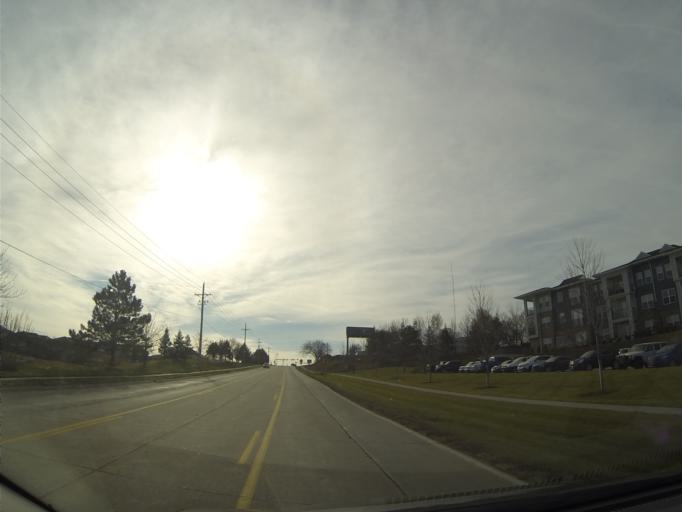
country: US
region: Nebraska
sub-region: Douglas County
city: Elkhorn
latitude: 41.2693
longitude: -96.2157
